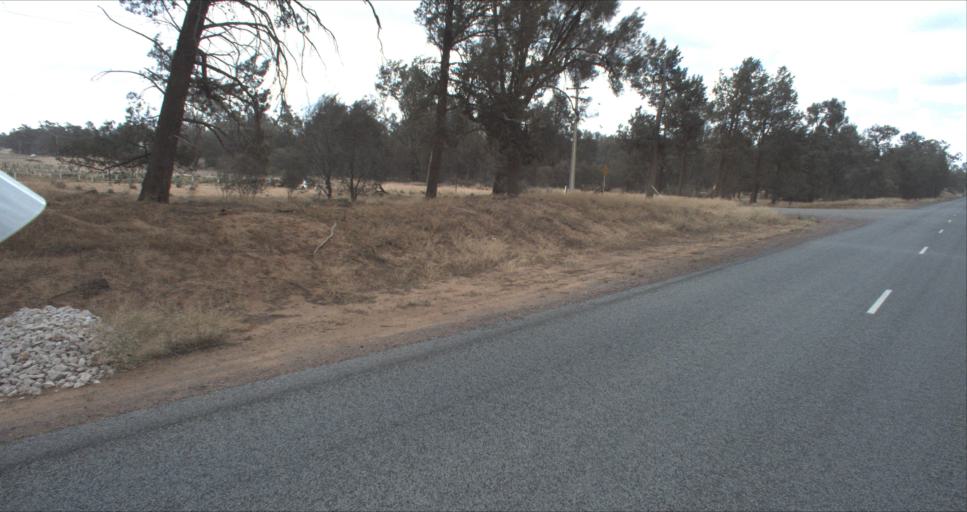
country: AU
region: New South Wales
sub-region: Leeton
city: Leeton
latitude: -34.6587
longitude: 146.3498
